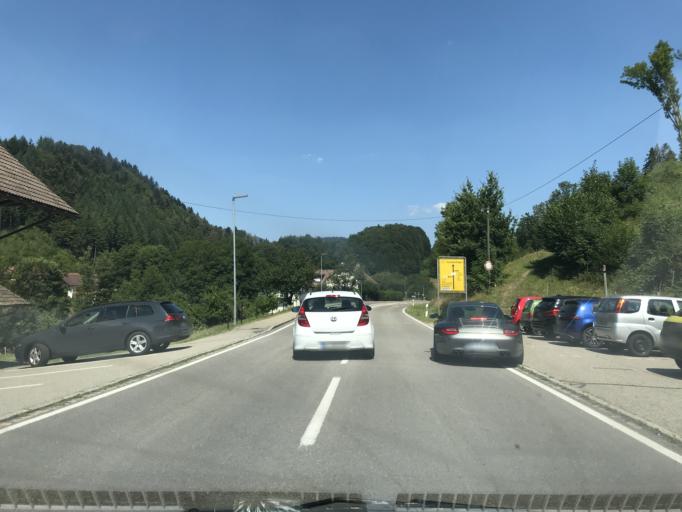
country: DE
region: Baden-Wuerttemberg
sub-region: Freiburg Region
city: Wembach
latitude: 47.7590
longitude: 7.8858
